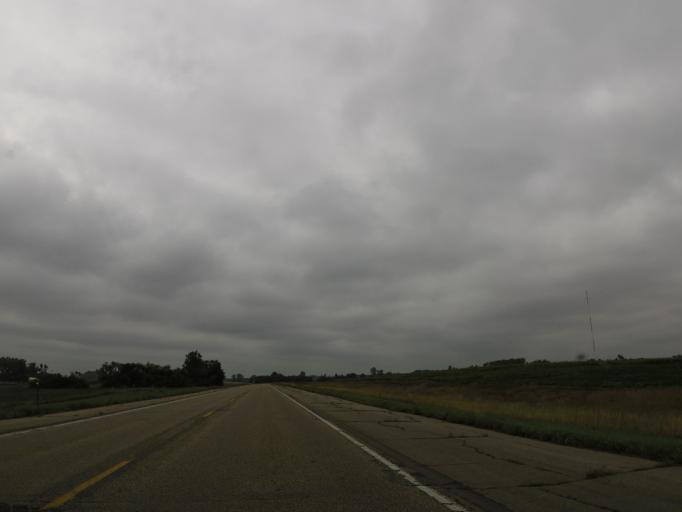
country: US
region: South Dakota
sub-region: Deuel County
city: Clear Lake
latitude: 44.9335
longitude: -96.6525
